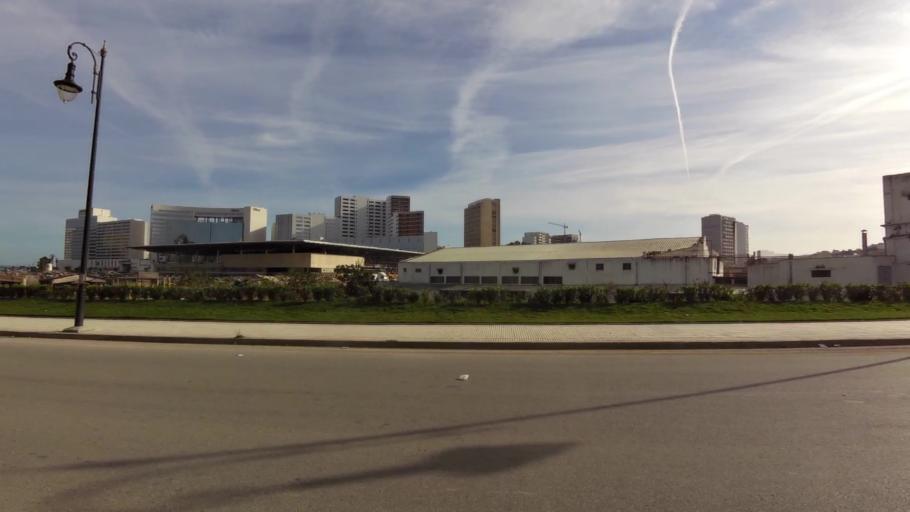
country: MA
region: Tanger-Tetouan
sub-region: Tanger-Assilah
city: Tangier
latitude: 35.7687
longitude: -5.7867
